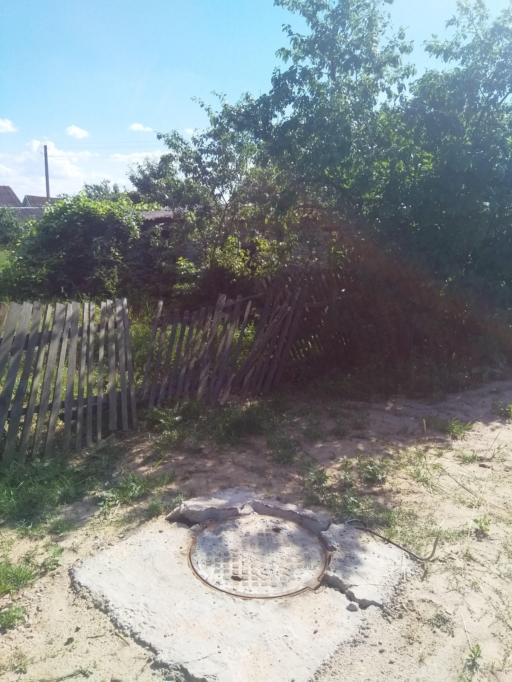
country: BY
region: Mogilev
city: Dashkawka
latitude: 53.7406
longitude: 30.2566
